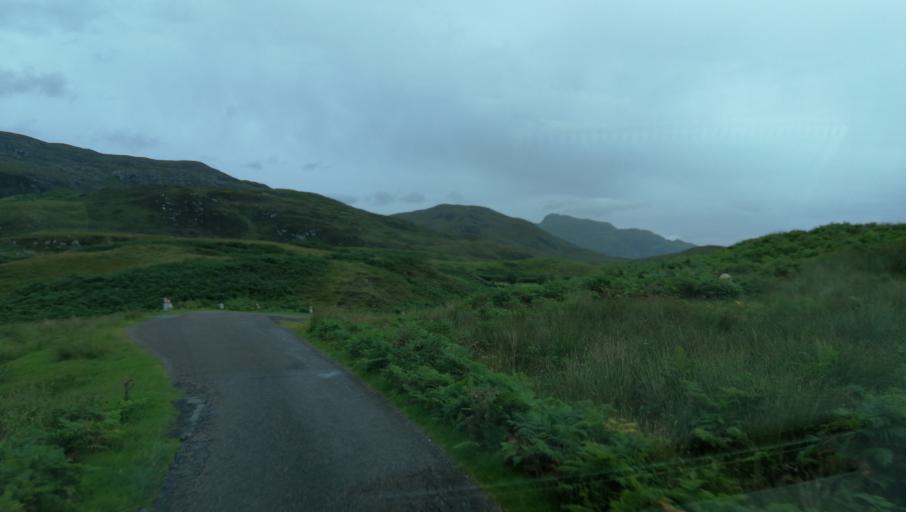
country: GB
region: Scotland
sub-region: Argyll and Bute
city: Isle Of Mull
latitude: 56.7092
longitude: -6.1359
